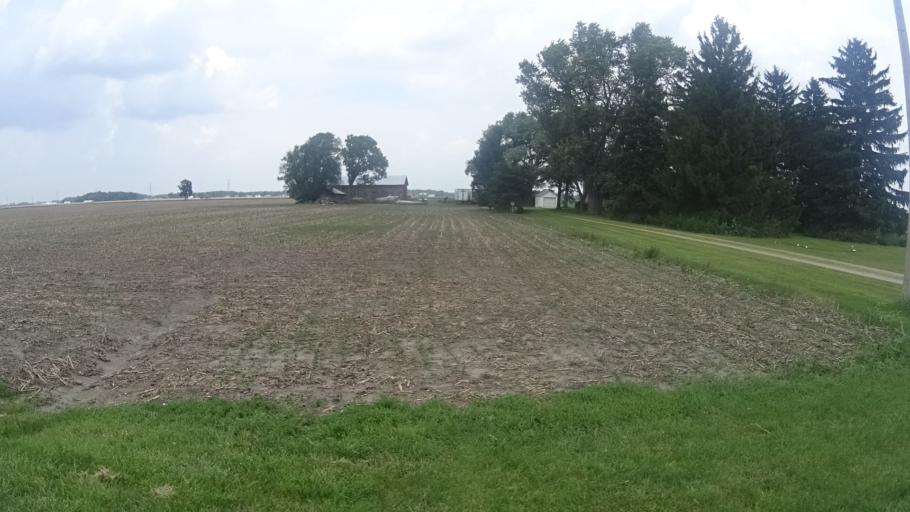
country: US
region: Ohio
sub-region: Erie County
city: Milan
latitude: 41.3228
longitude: -82.6517
